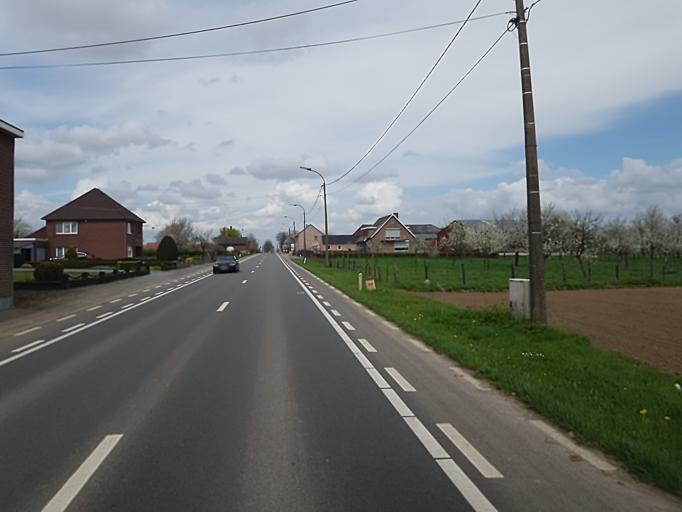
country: BE
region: Flanders
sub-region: Provincie Limburg
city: Riemst
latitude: 50.8331
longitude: 5.6256
